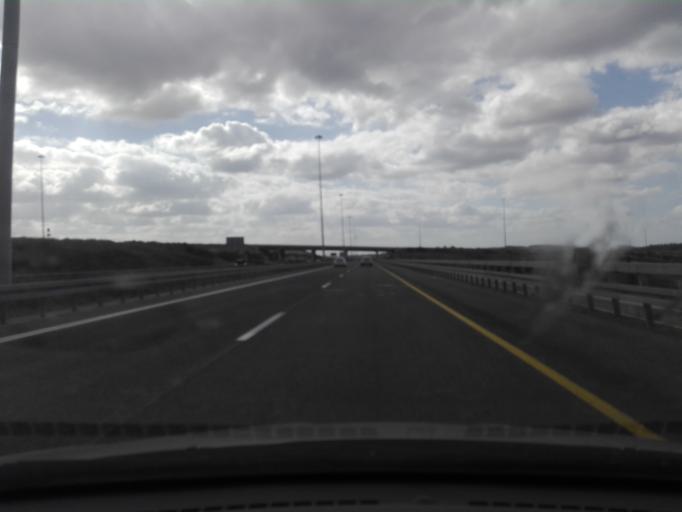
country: IL
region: Haifa
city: Daliyat el Karmil
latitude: 32.6131
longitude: 35.0498
